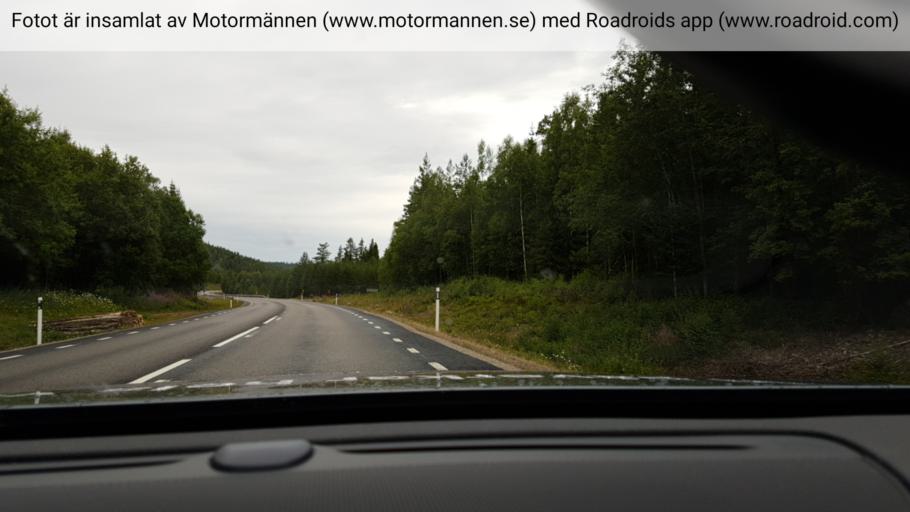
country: SE
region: Dalarna
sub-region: Rattviks Kommun
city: Raettvik
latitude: 60.7979
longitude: 15.2709
